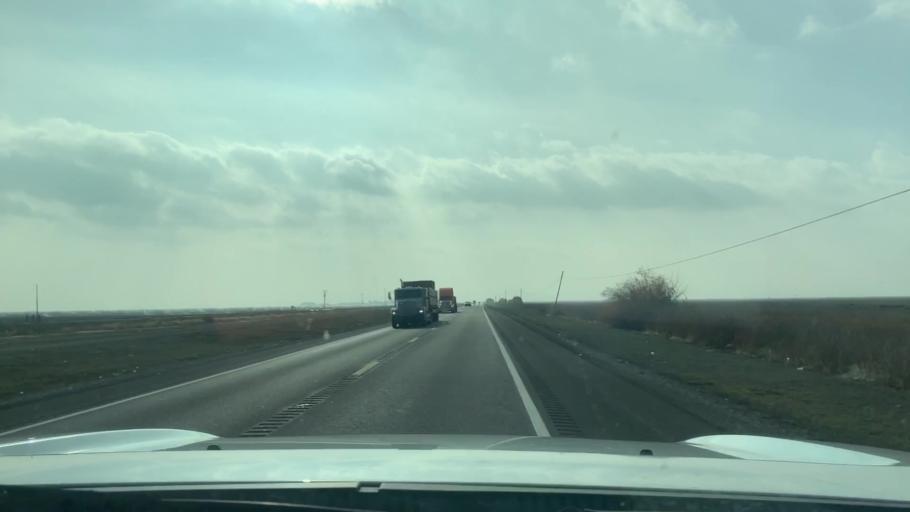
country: US
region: California
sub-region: Kings County
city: Stratford
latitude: 36.1579
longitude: -119.8552
